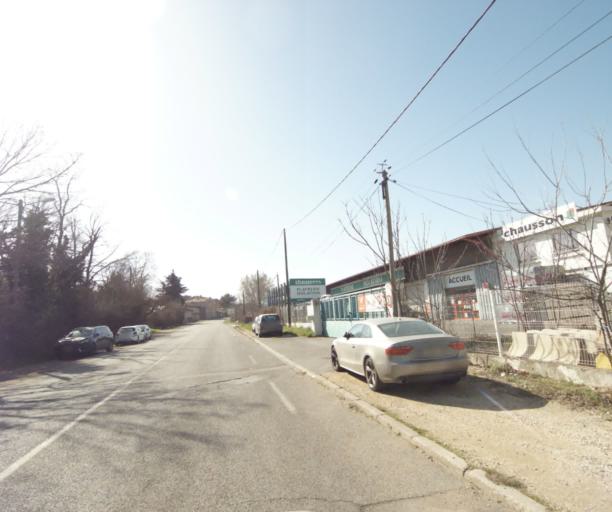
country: FR
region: Provence-Alpes-Cote d'Azur
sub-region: Departement des Bouches-du-Rhone
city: Cabries
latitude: 43.4209
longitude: 5.3830
